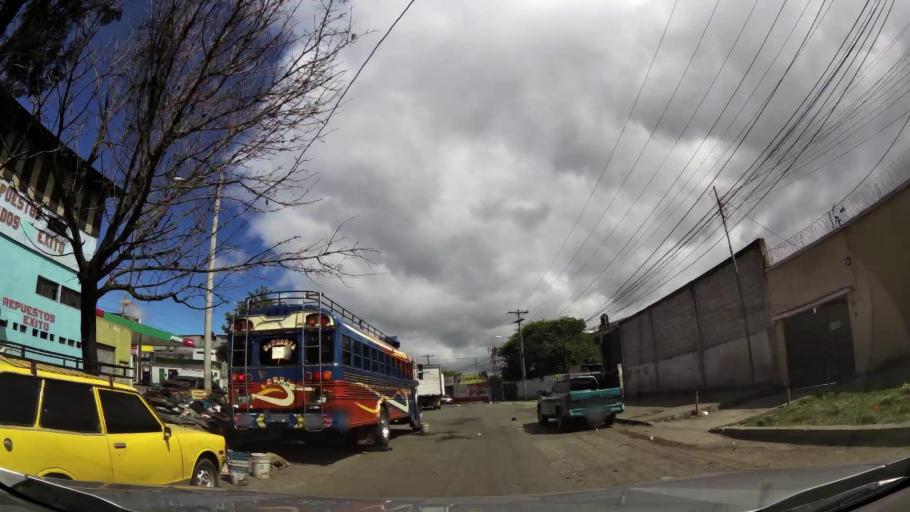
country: GT
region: Guatemala
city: Guatemala City
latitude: 14.6124
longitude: -90.5256
